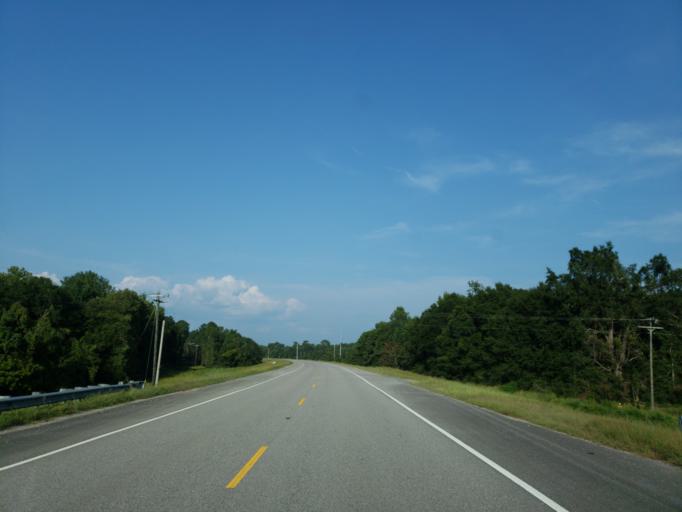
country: US
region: Alabama
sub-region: Sumter County
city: Livingston
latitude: 32.6989
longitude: -88.0959
